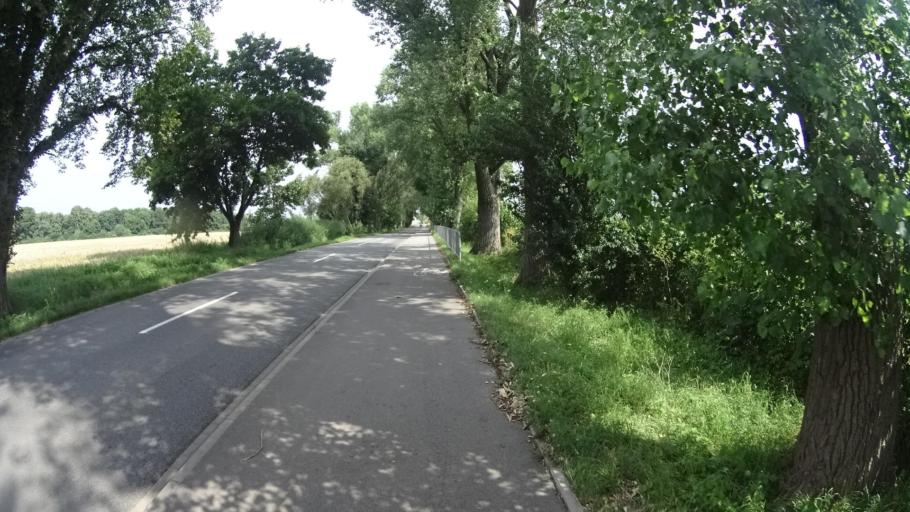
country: PL
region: Masovian Voivodeship
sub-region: Powiat pruszkowski
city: Nadarzyn
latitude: 52.0576
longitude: 20.7857
